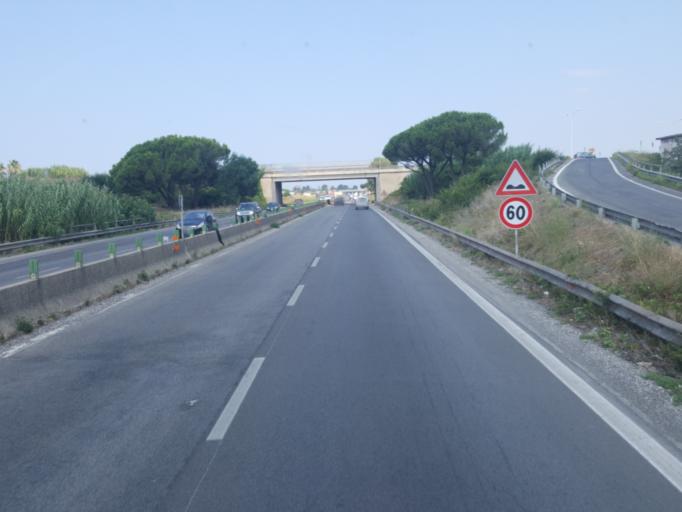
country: IT
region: Latium
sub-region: Provincia di Latina
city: Aprilia
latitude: 41.5715
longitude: 12.6649
